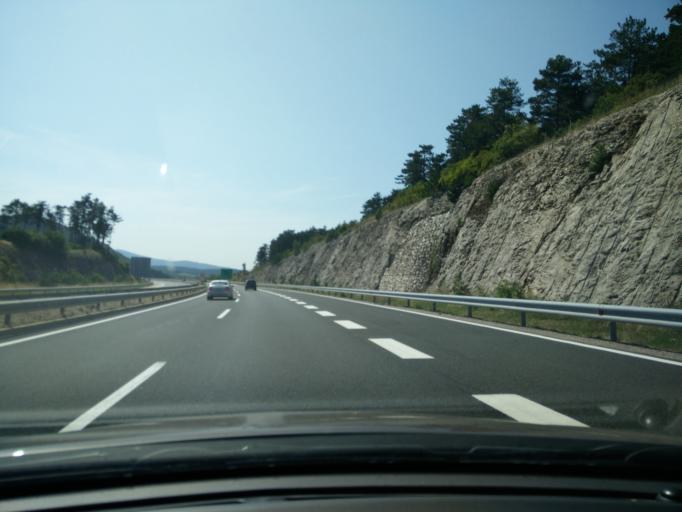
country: SI
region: Hrpelje-Kozina
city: Kozina
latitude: 45.6053
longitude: 13.9279
